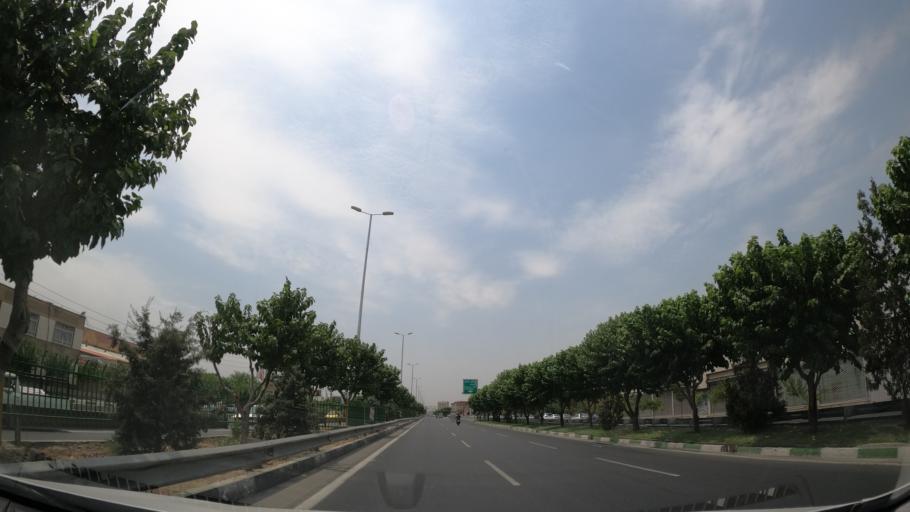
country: IR
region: Tehran
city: Tehran
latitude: 35.6751
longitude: 51.3207
